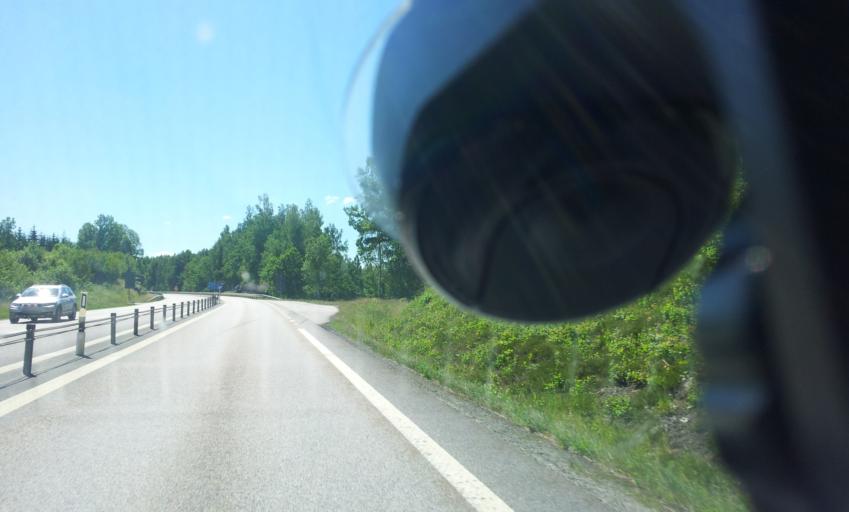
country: SE
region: Kalmar
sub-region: Vasterviks Kommun
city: Forserum
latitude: 58.0810
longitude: 16.5198
